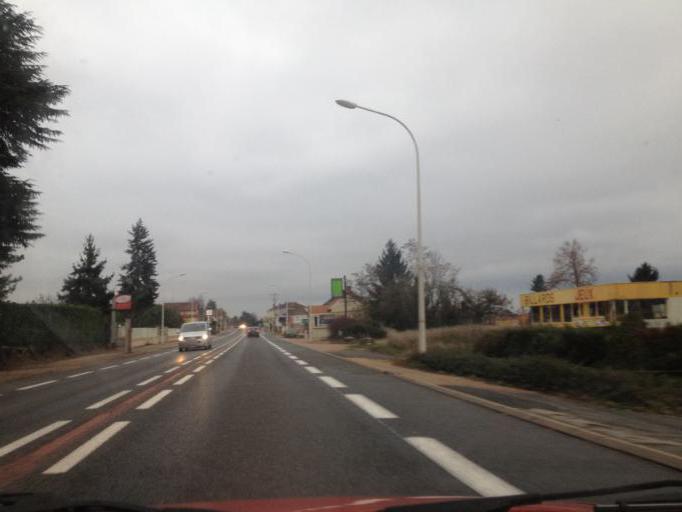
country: FR
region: Auvergne
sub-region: Departement de l'Allier
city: Varennes-sur-Allier
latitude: 46.3234
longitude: 3.3905
